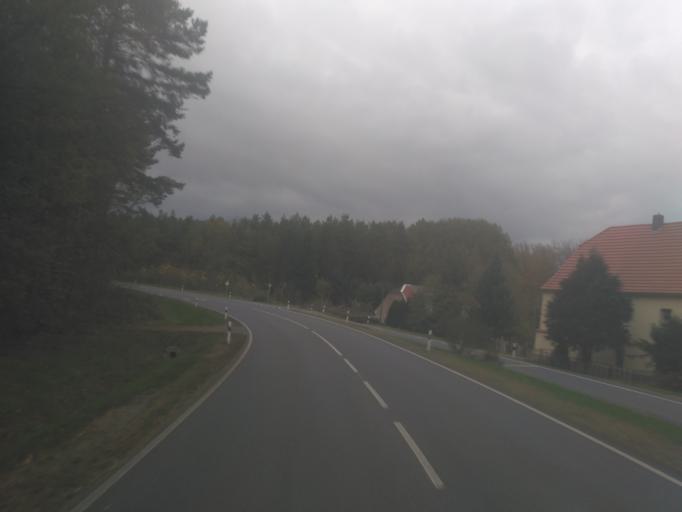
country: DE
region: Brandenburg
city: Merzdorf
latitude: 51.4014
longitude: 13.5040
